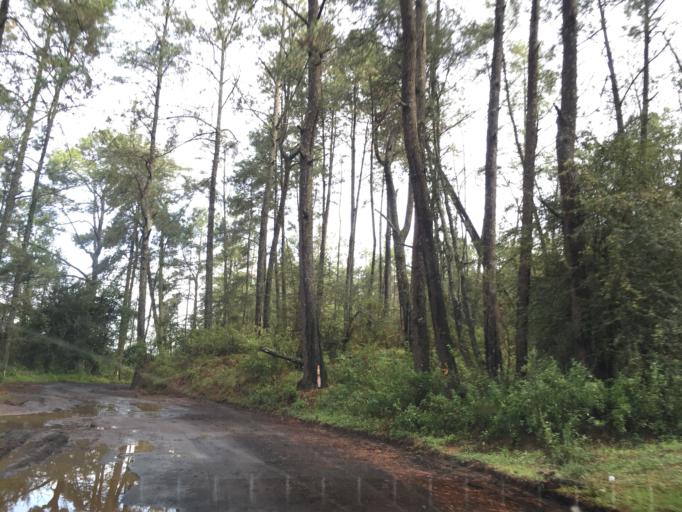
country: MX
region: Michoacan
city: Angahuan
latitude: 19.5162
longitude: -102.2200
